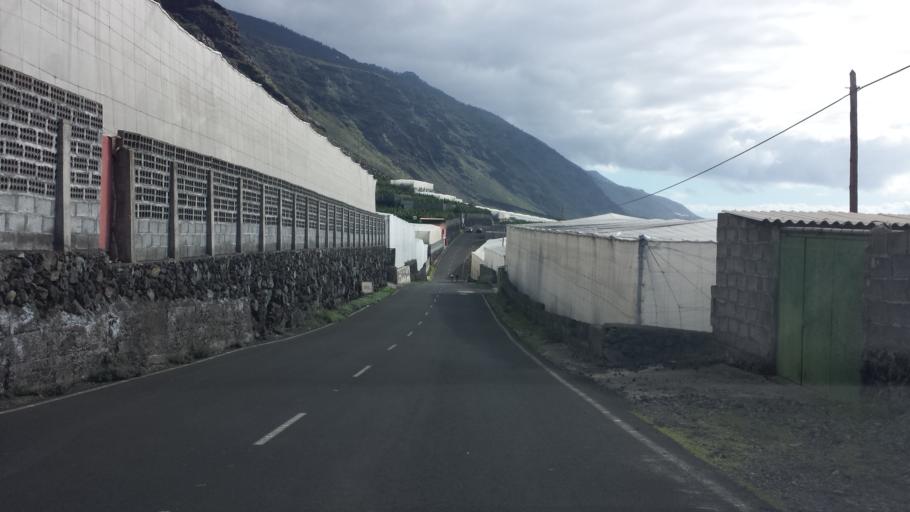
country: ES
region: Canary Islands
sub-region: Provincia de Santa Cruz de Tenerife
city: El Paso
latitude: 28.5679
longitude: -17.8941
